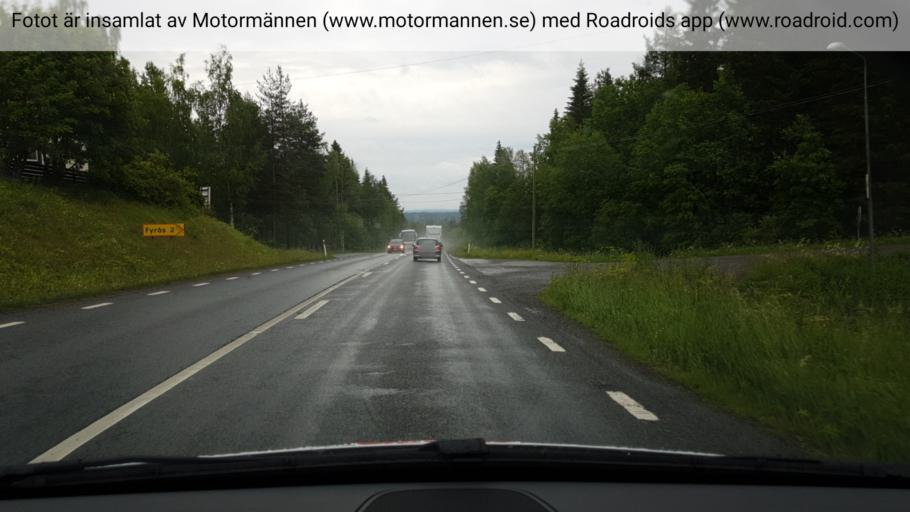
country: SE
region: Jaemtland
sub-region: Stroemsunds Kommun
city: Stroemsund
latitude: 63.5346
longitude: 15.3377
